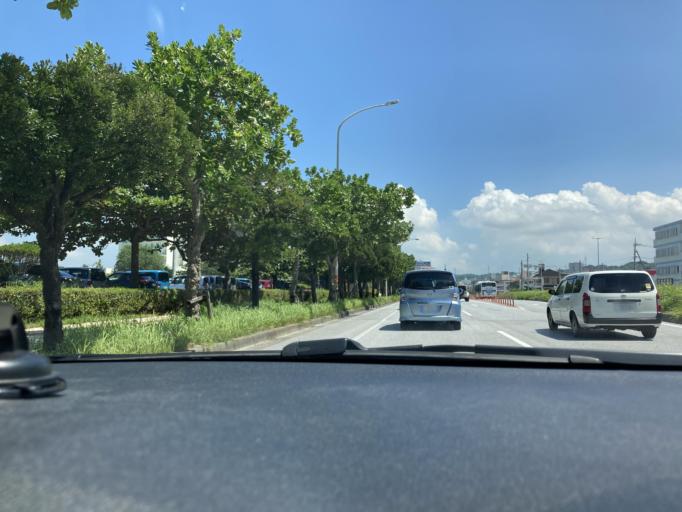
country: JP
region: Okinawa
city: Ginowan
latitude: 26.2792
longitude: 127.7358
